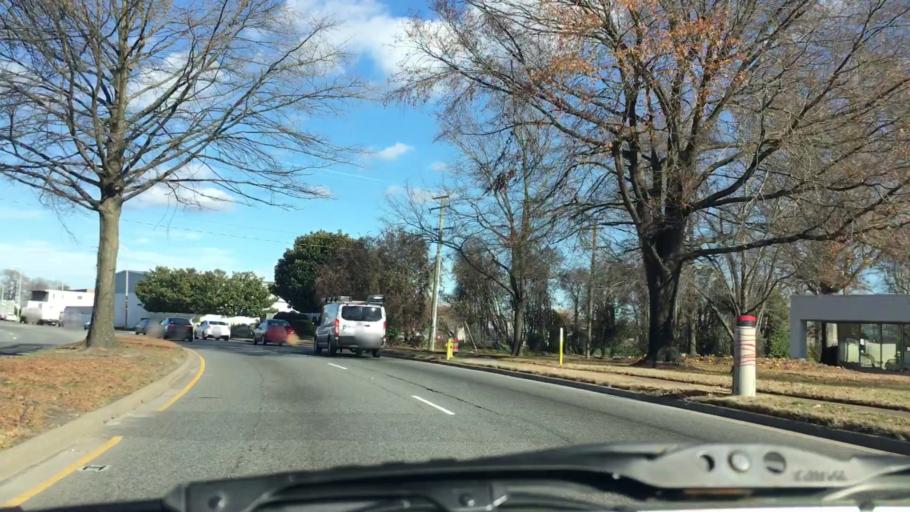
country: US
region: Virginia
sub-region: City of Norfolk
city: Norfolk
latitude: 36.8504
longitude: -76.2482
